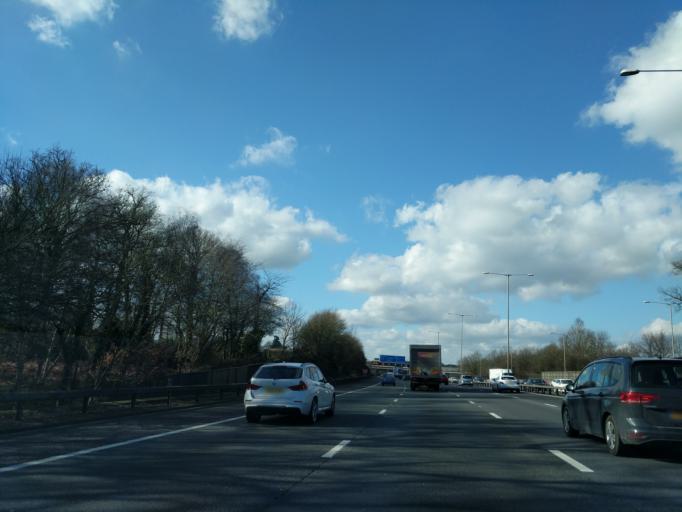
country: GB
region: England
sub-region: Buckinghamshire
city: Denham
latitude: 51.5457
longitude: -0.5100
